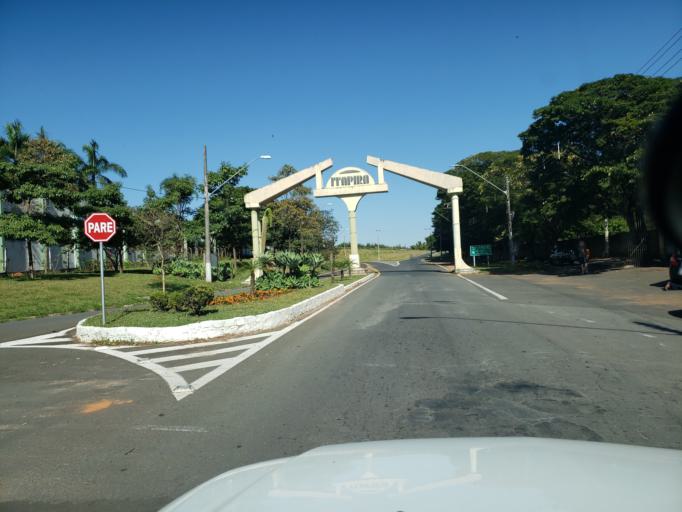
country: BR
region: Sao Paulo
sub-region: Itapira
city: Itapira
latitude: -22.4449
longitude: -46.8318
